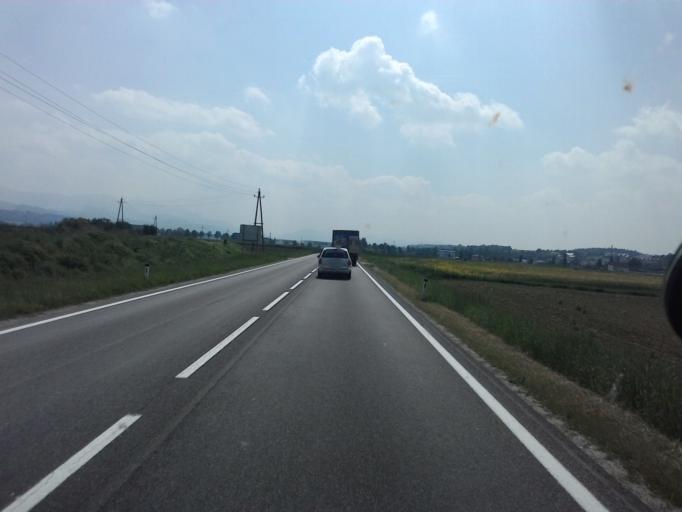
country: AT
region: Upper Austria
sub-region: Politischer Bezirk Steyr-Land
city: Sierning
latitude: 48.0442
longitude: 14.3213
